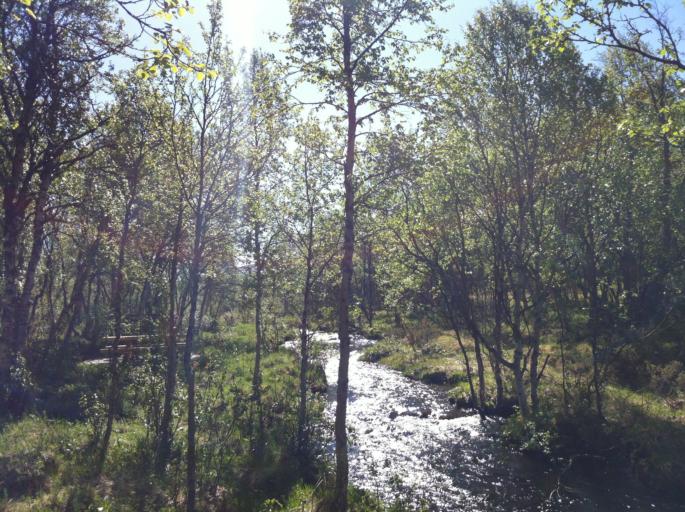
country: NO
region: Sor-Trondelag
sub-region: Roros
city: Roros
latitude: 62.6031
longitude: 11.6605
